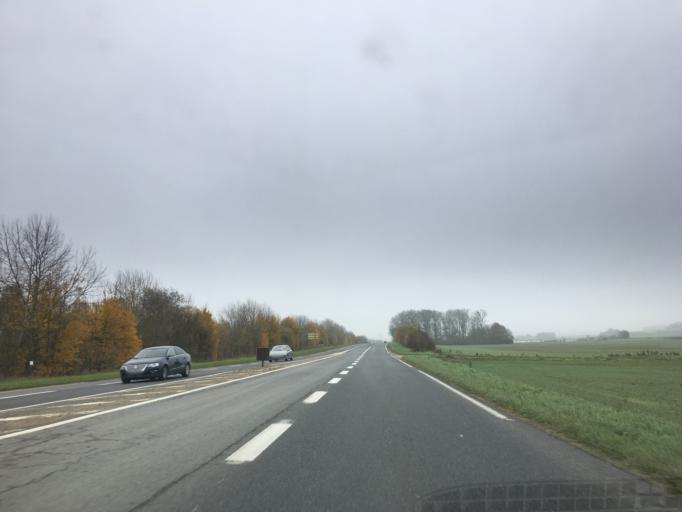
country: FR
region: Ile-de-France
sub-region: Departement de Seine-et-Marne
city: La Grande-Paroisse
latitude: 48.3612
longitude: 2.8888
